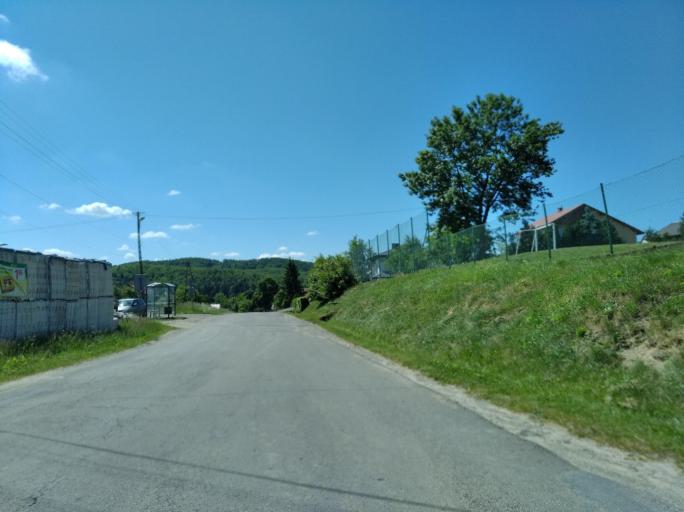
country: PL
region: Subcarpathian Voivodeship
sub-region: Powiat krosnienski
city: Chorkowka
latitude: 49.6424
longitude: 21.6104
